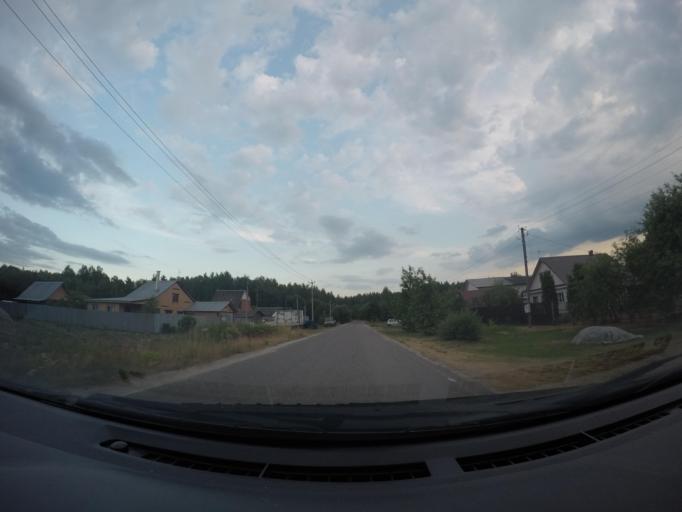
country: RU
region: Moskovskaya
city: Krasnyy Tkach
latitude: 55.3814
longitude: 39.2047
